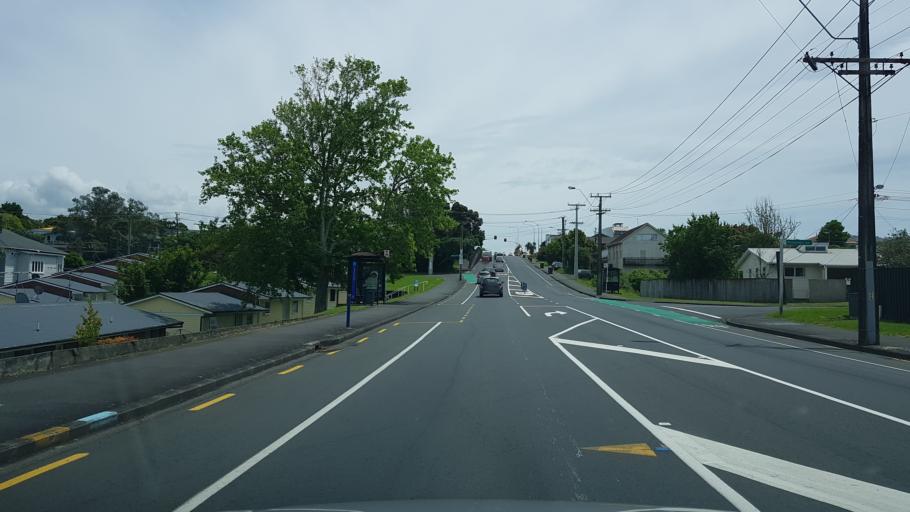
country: NZ
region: Auckland
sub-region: Auckland
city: North Shore
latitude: -36.8106
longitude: 174.7912
